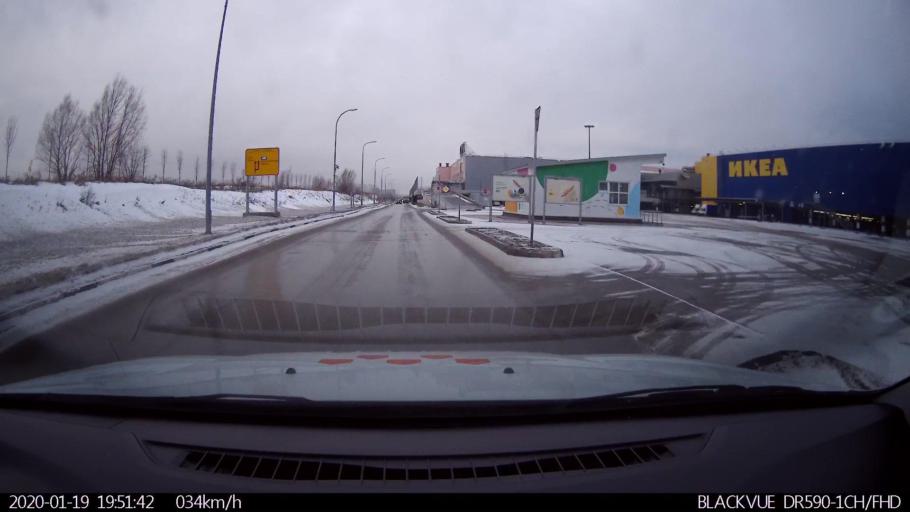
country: RU
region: Nizjnij Novgorod
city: Afonino
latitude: 56.2226
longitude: 44.0698
